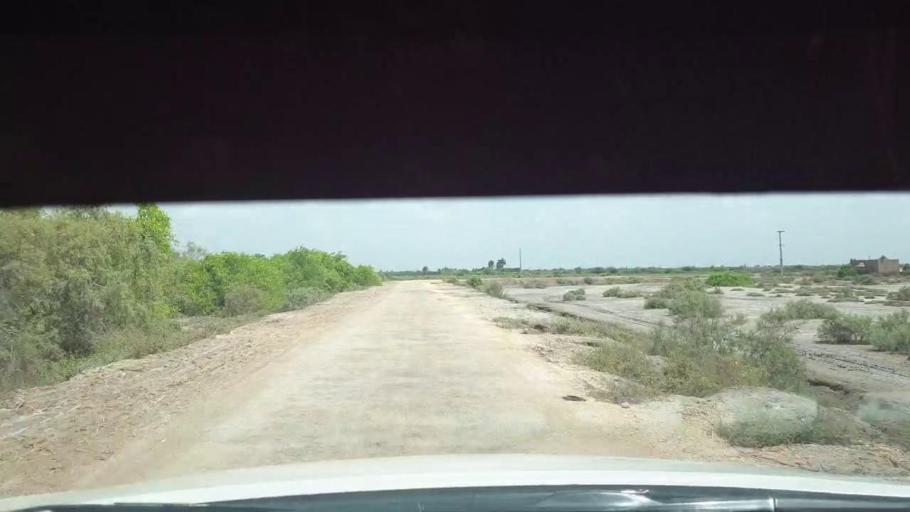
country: PK
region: Sindh
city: Kadhan
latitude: 24.5192
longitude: 68.9700
